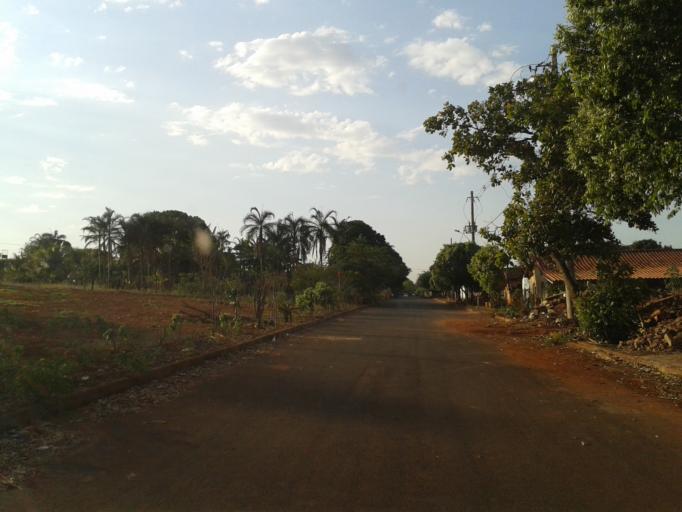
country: BR
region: Minas Gerais
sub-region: Ituiutaba
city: Ituiutaba
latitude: -18.9898
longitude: -49.4422
